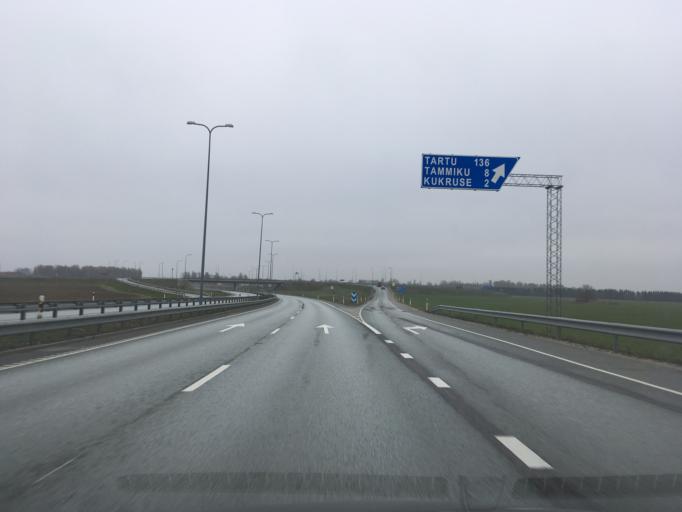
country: EE
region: Ida-Virumaa
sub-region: Kohtla-Jaerve linn
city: Kohtla-Jarve
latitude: 59.3885
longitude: 27.3419
